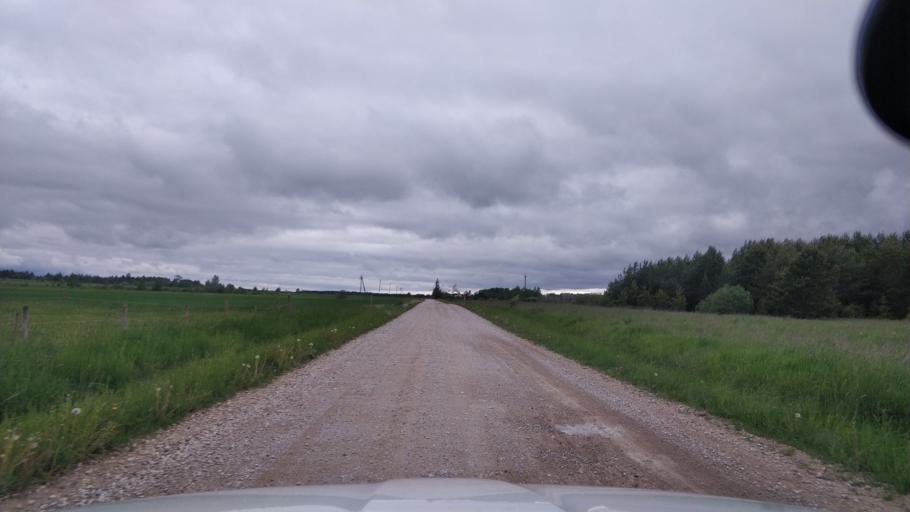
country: EE
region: Raplamaa
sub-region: Maerjamaa vald
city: Marjamaa
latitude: 58.7146
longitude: 24.2461
